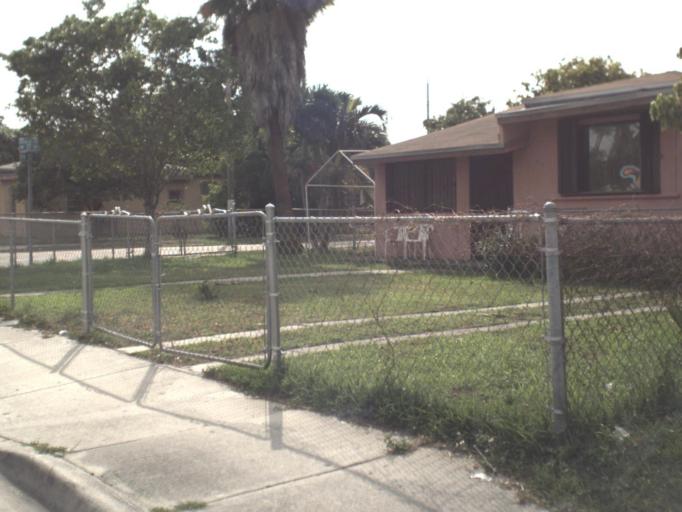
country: US
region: Florida
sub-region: Miami-Dade County
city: Brownsville
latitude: 25.7837
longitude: -80.2559
